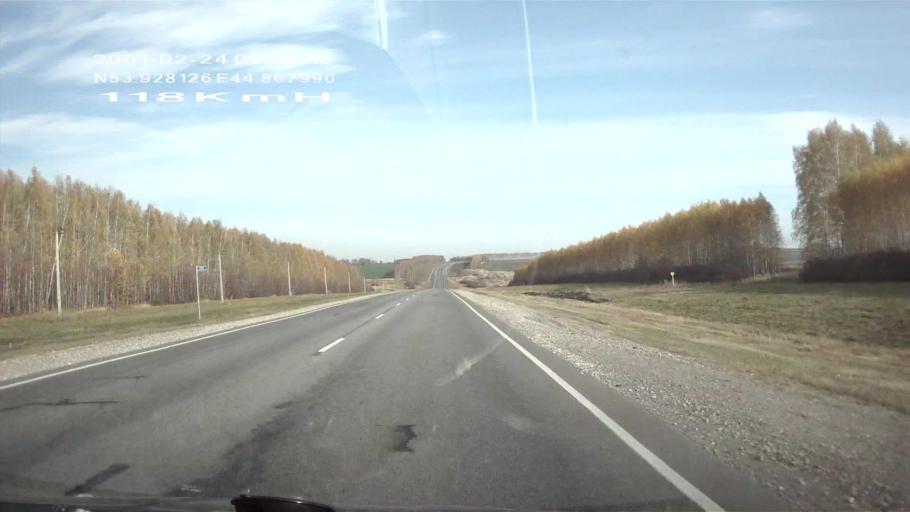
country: RU
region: Penza
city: Issa
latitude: 53.9284
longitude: 44.8682
